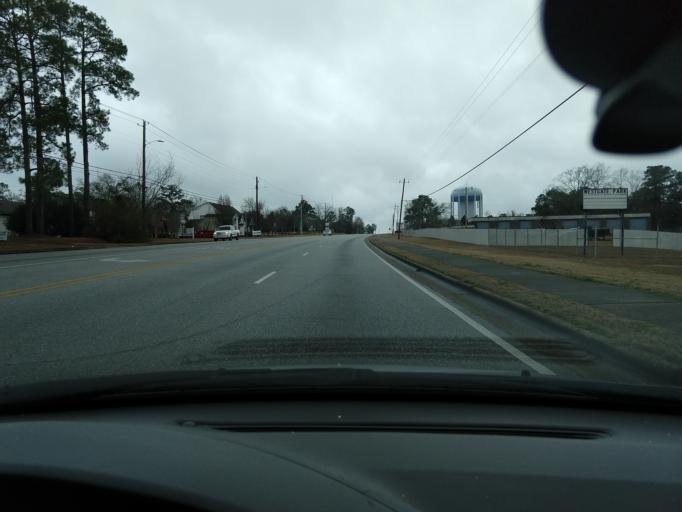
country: US
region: Alabama
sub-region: Houston County
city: Dothan
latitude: 31.2391
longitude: -85.4348
